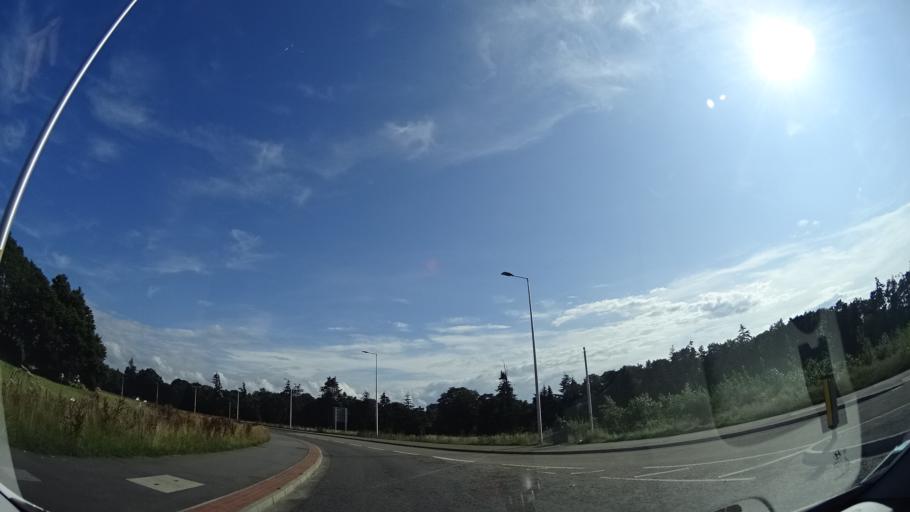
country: GB
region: Scotland
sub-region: Highland
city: Inverness
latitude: 57.4524
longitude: -4.2564
